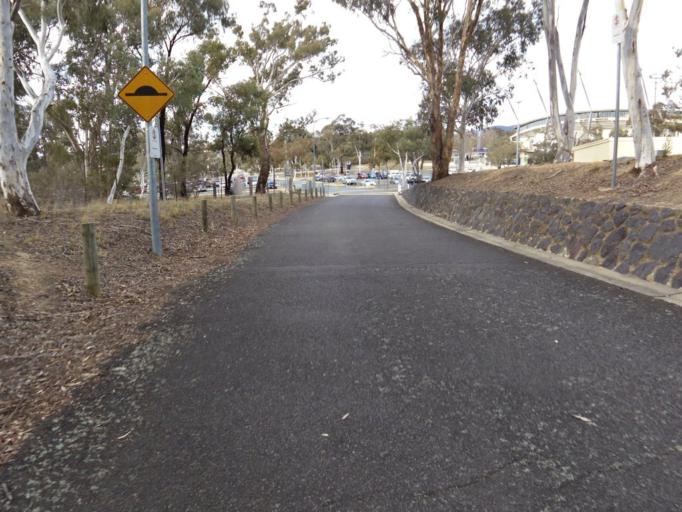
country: AU
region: Australian Capital Territory
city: Kaleen
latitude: -35.2497
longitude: 149.0992
